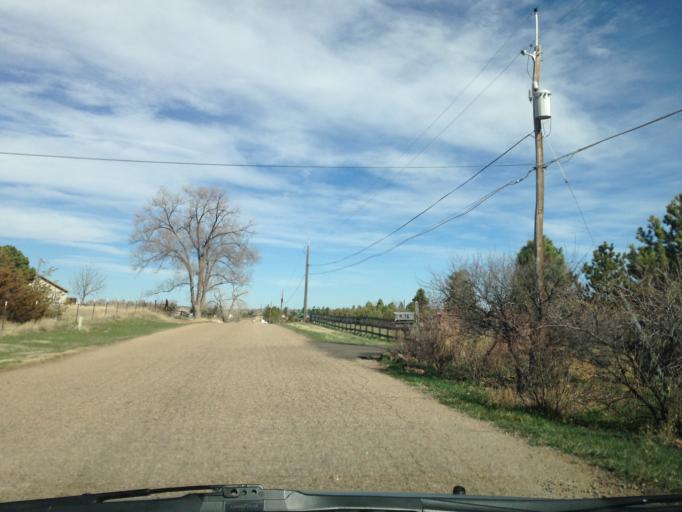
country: US
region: Colorado
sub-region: Boulder County
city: Gunbarrel
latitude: 40.0619
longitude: -105.1263
